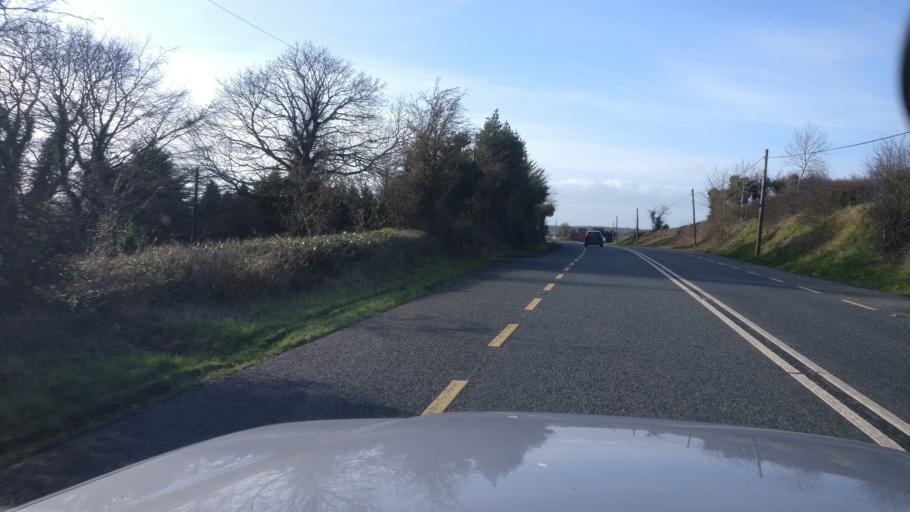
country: IE
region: Leinster
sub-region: Uibh Fhaili
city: Tullamore
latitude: 53.2173
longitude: -7.4657
